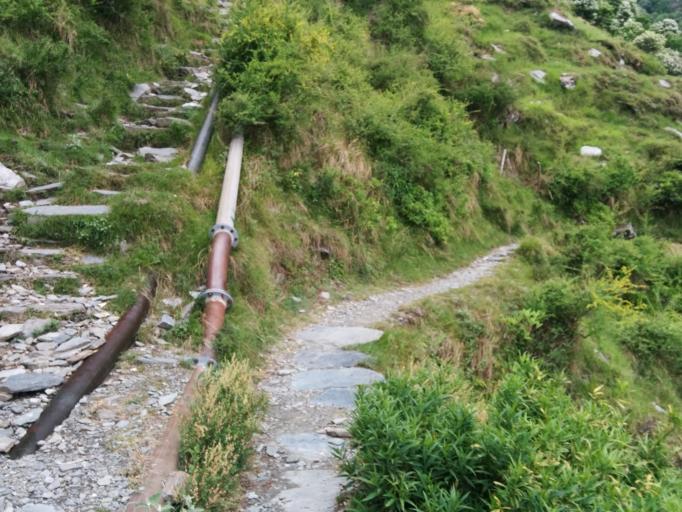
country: IN
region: Himachal Pradesh
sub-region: Kangra
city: Dharmsala
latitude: 32.2477
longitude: 76.3377
